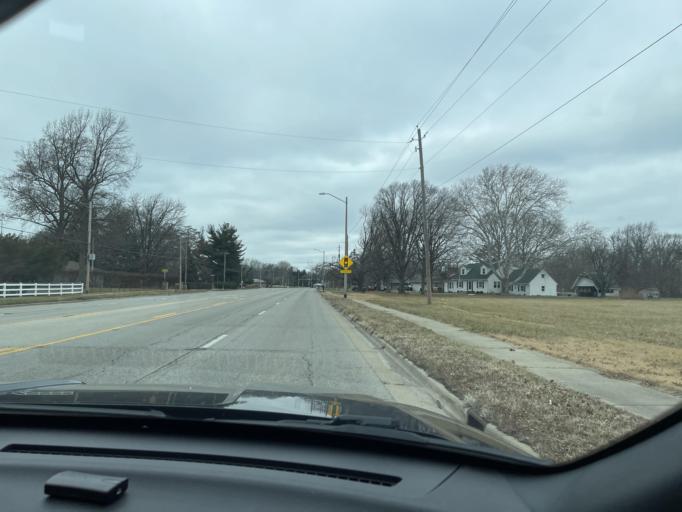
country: US
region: Illinois
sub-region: Sangamon County
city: Leland Grove
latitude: 39.8107
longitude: -89.6905
